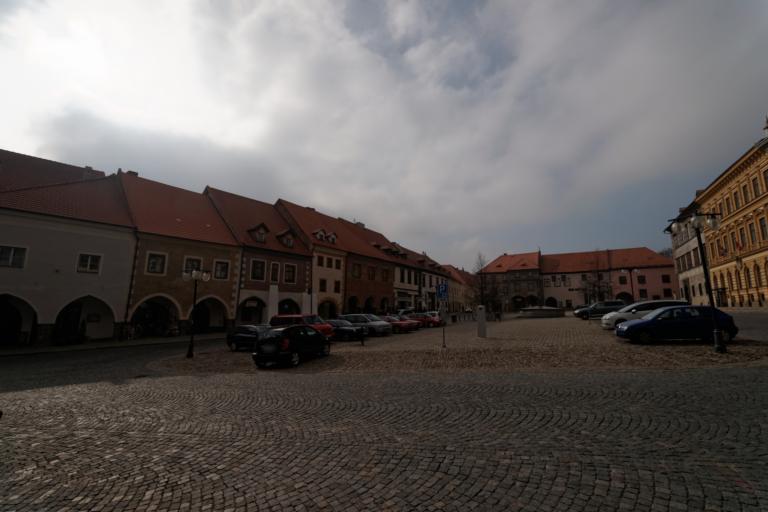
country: CZ
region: Jihocesky
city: Prachatice
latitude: 49.0132
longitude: 13.9980
